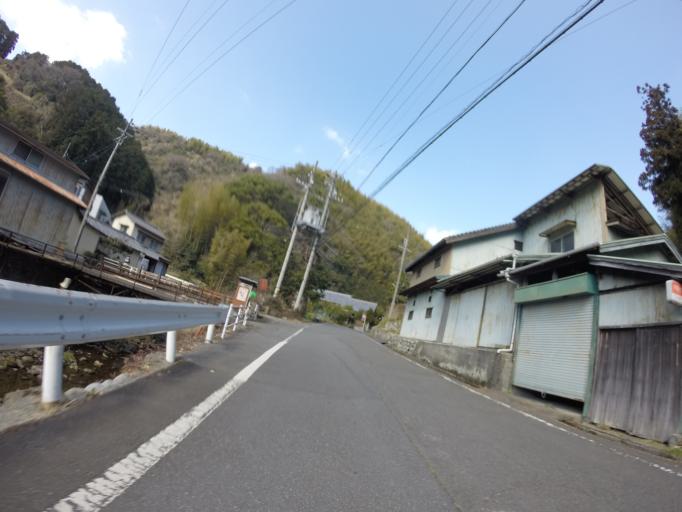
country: JP
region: Shizuoka
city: Shizuoka-shi
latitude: 35.0589
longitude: 138.4978
